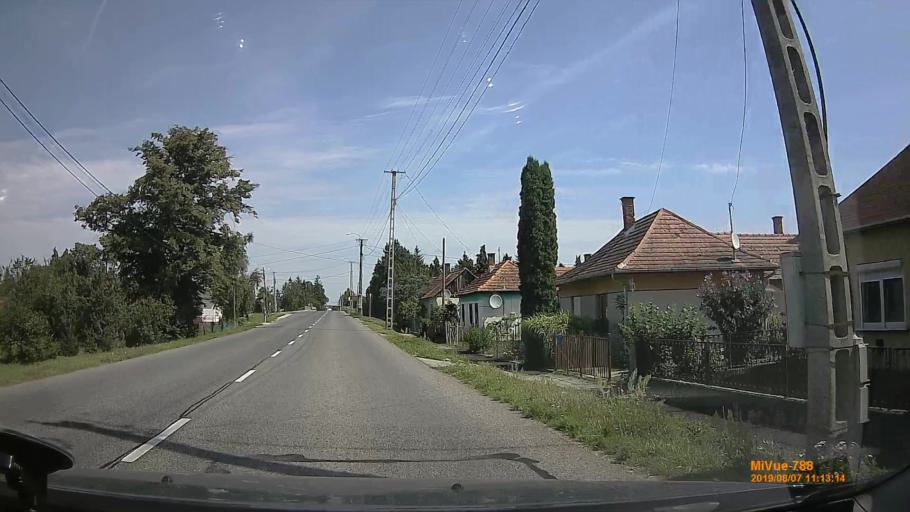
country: HU
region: Zala
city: Lenti
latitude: 46.6981
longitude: 16.5472
